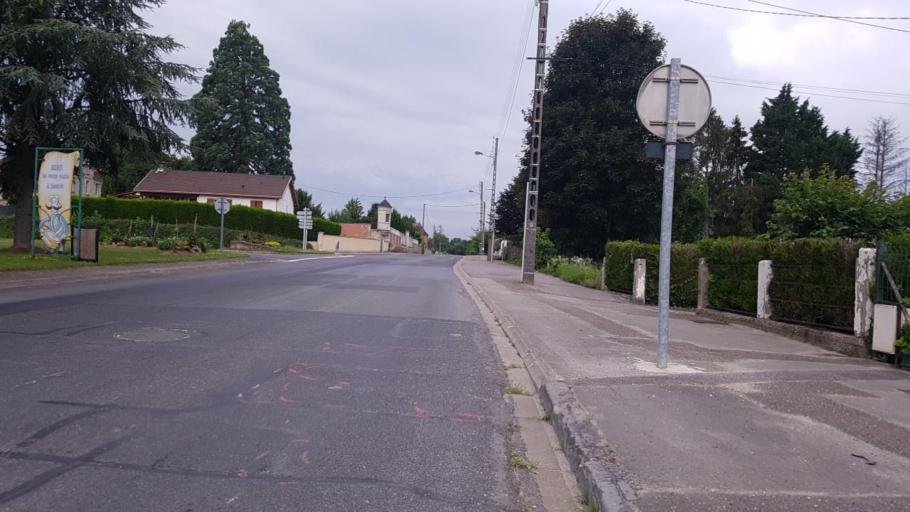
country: FR
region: Champagne-Ardenne
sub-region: Departement de la Marne
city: Sermaize-les-Bains
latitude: 48.7816
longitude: 4.9040
